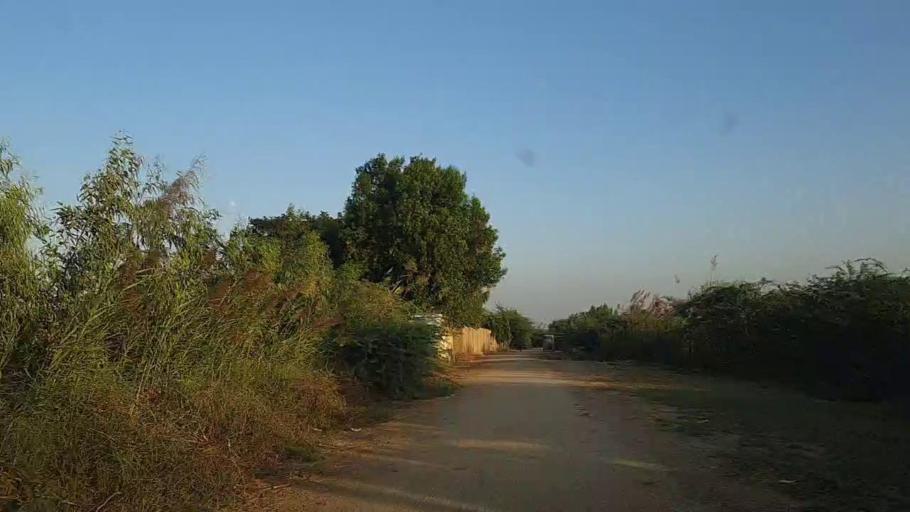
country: PK
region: Sindh
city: Thatta
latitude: 24.7584
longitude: 67.9324
